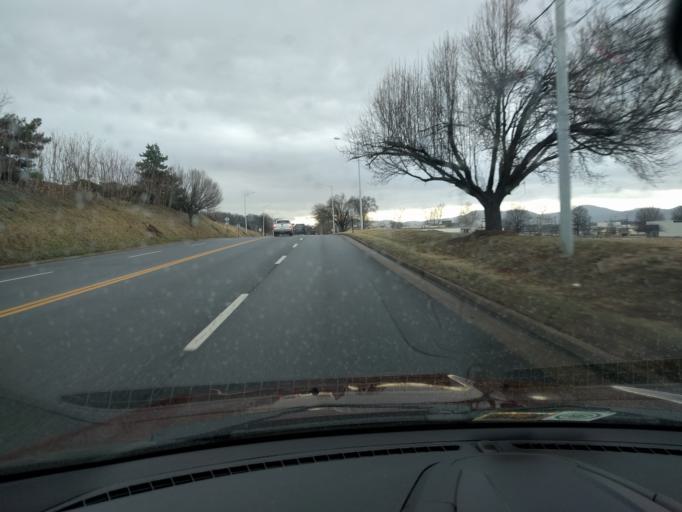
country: US
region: Virginia
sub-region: Roanoke County
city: Hollins
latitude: 37.3101
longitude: -79.9643
